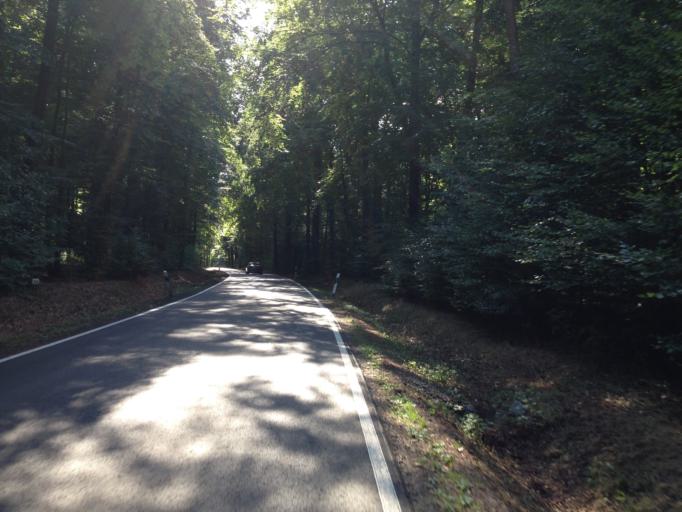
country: DE
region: Hesse
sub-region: Regierungsbezirk Giessen
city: Reiskirchen
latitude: 50.6211
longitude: 8.8849
